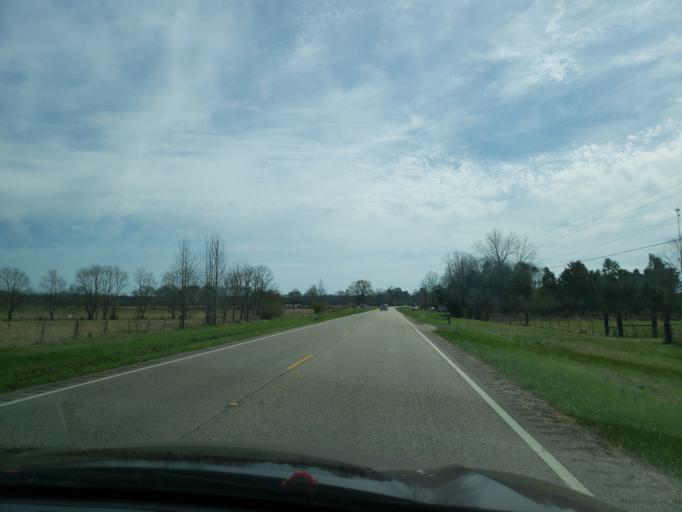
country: US
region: Alabama
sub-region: Dallas County
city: Selma
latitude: 32.4705
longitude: -87.1022
